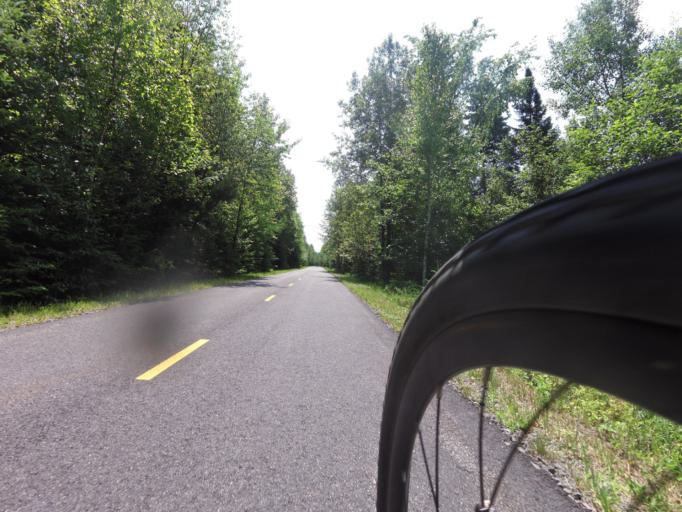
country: CA
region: Quebec
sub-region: Laurentides
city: Mont-Tremblant
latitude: 46.1484
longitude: -74.5938
